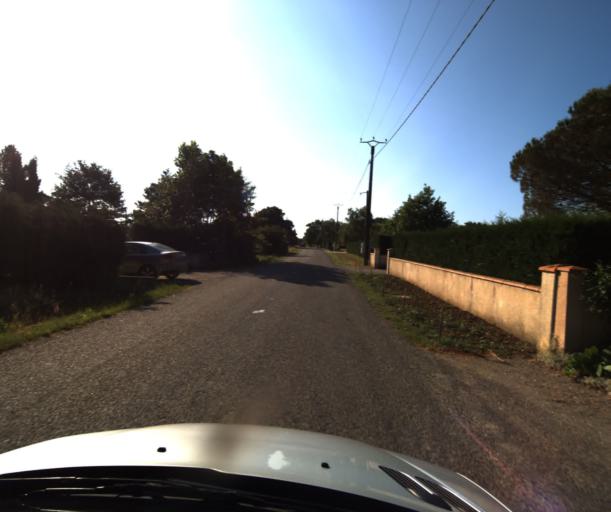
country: FR
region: Midi-Pyrenees
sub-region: Departement du Tarn-et-Garonne
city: Saint-Porquier
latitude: 44.0707
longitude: 1.1989
